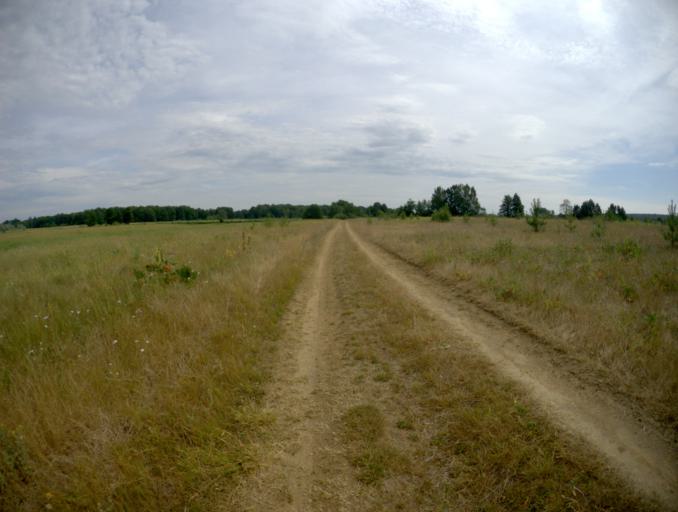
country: RU
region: Vladimir
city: Raduzhnyy
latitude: 56.0308
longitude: 40.2748
